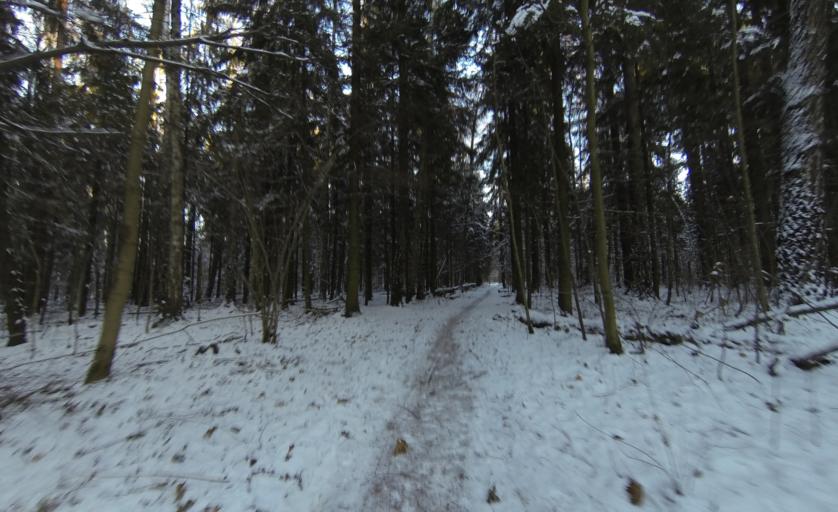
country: RU
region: Moscow
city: Gol'yanovo
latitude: 55.8486
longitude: 37.7844
